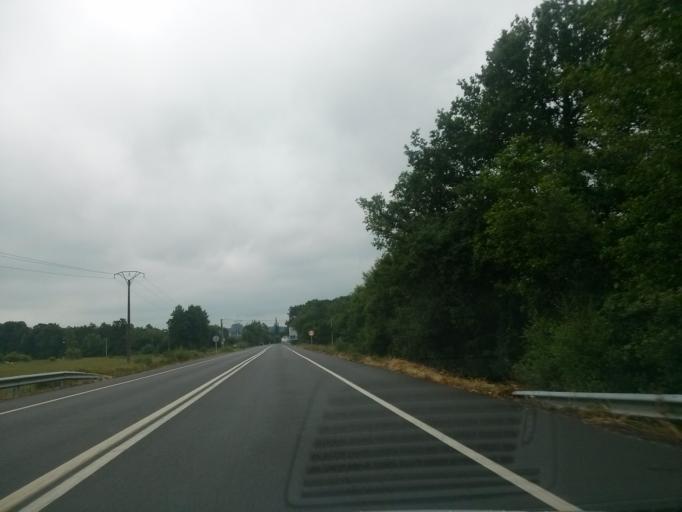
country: ES
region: Galicia
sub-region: Provincia de Lugo
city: Begonte
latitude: 43.1620
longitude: -7.7013
